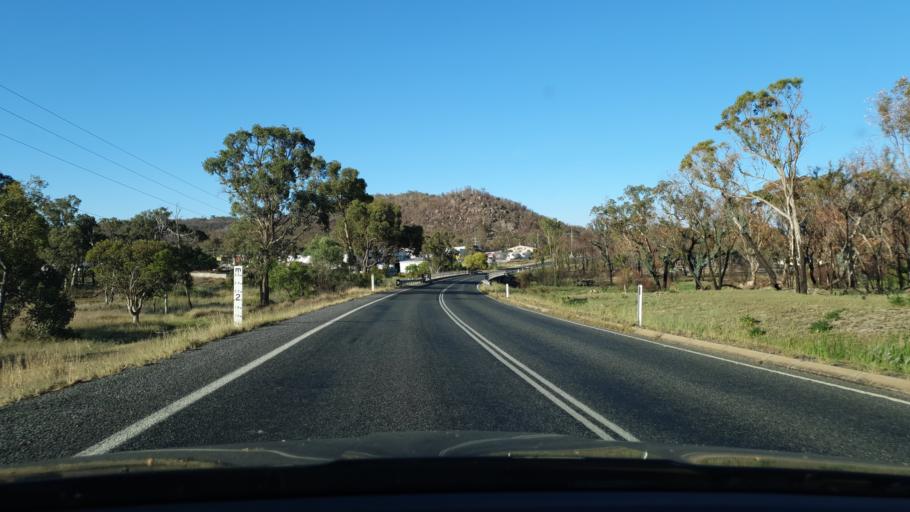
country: AU
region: Queensland
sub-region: Southern Downs
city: Stanthorpe
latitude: -28.6546
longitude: 151.9177
